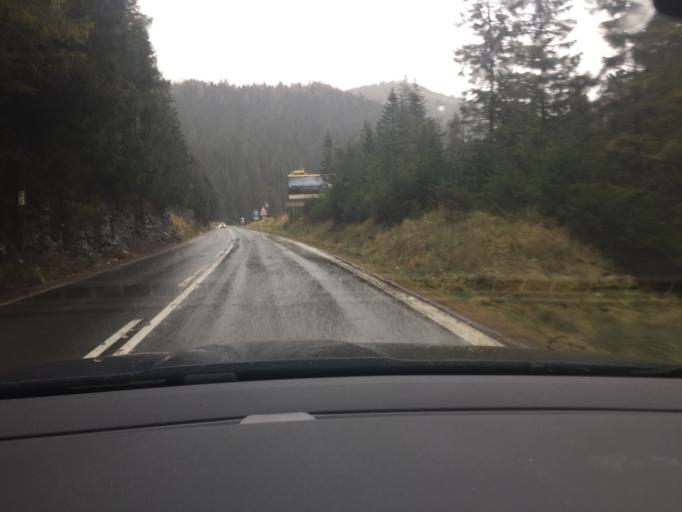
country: SK
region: Presovsky
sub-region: Okres Poprad
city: Zdiar
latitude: 49.2647
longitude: 20.2966
